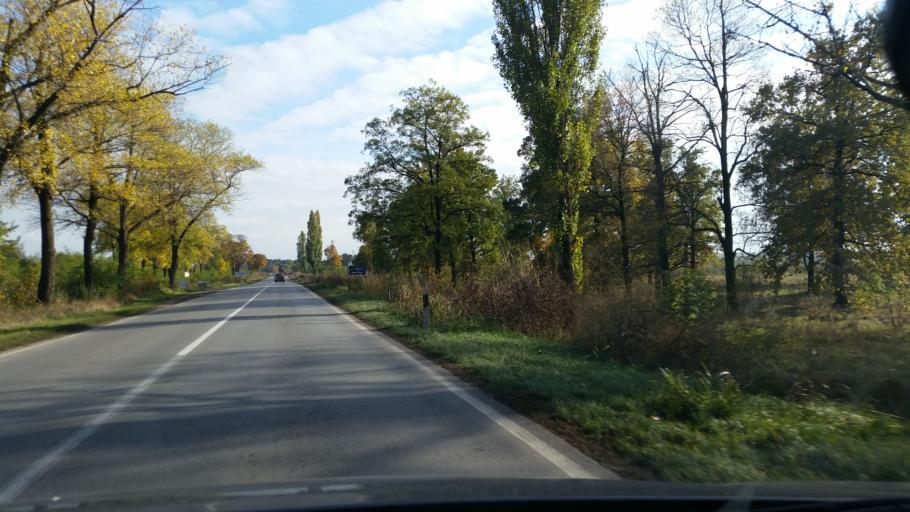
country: RS
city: Ecka
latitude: 45.3369
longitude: 20.4341
